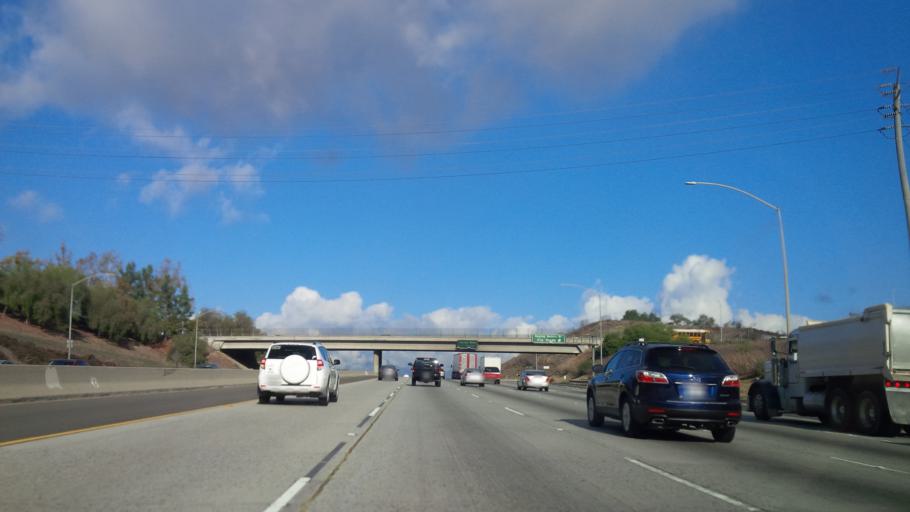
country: US
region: California
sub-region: Los Angeles County
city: San Dimas
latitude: 34.0766
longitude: -117.8126
